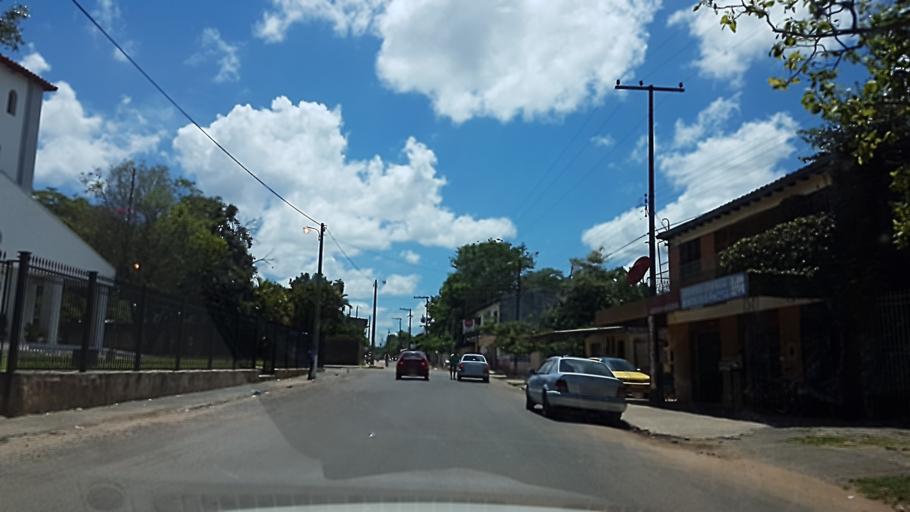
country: PY
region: Central
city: Colonia Mariano Roque Alonso
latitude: -25.2418
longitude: -57.5308
